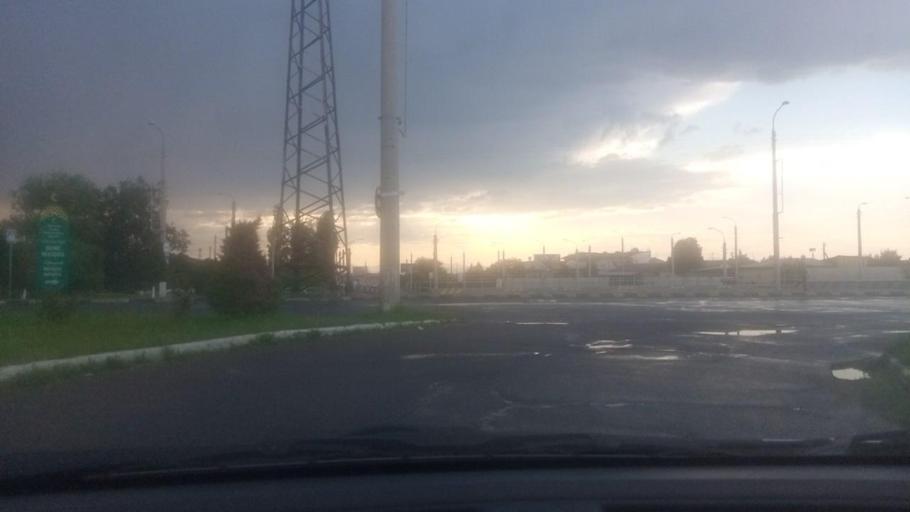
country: UZ
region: Toshkent Shahri
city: Tashkent
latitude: 41.3181
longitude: 69.1927
